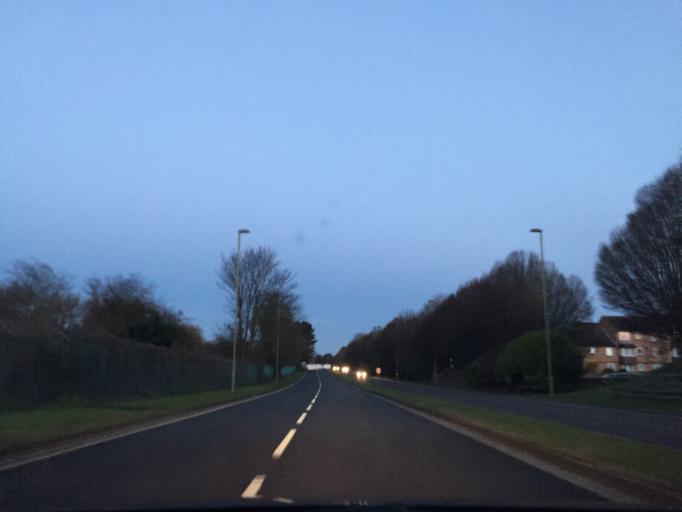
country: GB
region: England
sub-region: Hampshire
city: Fareham
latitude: 50.8510
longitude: -1.1826
